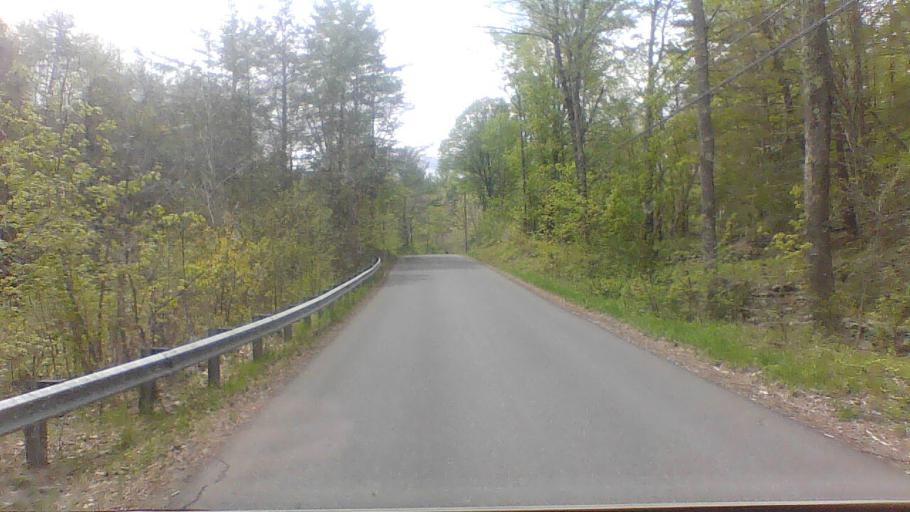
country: US
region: Massachusetts
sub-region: Franklin County
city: Buckland
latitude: 42.5807
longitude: -72.8225
